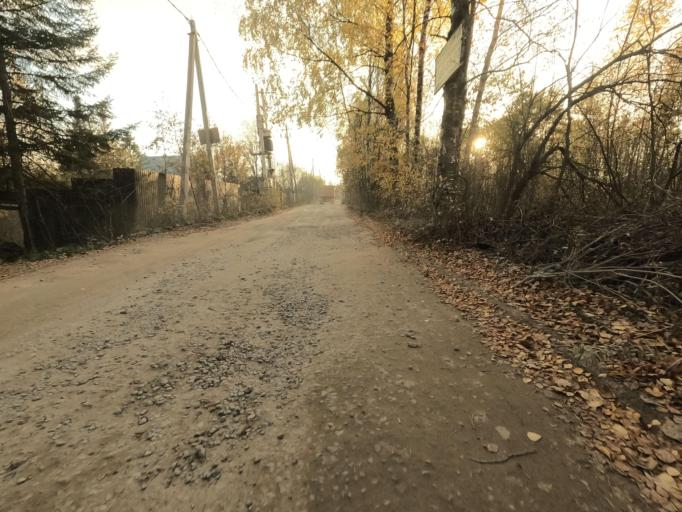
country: RU
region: St.-Petersburg
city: Beloostrov
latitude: 60.1799
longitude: 30.0412
